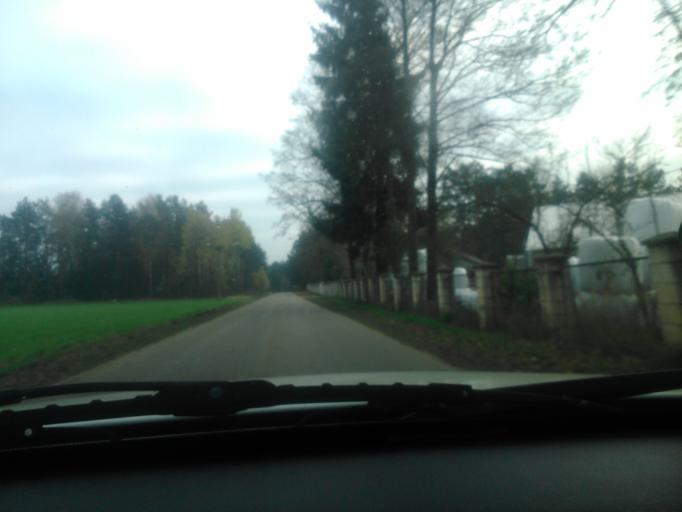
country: PL
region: Masovian Voivodeship
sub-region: Powiat ostrolecki
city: Czarnia
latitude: 53.3595
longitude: 21.1933
